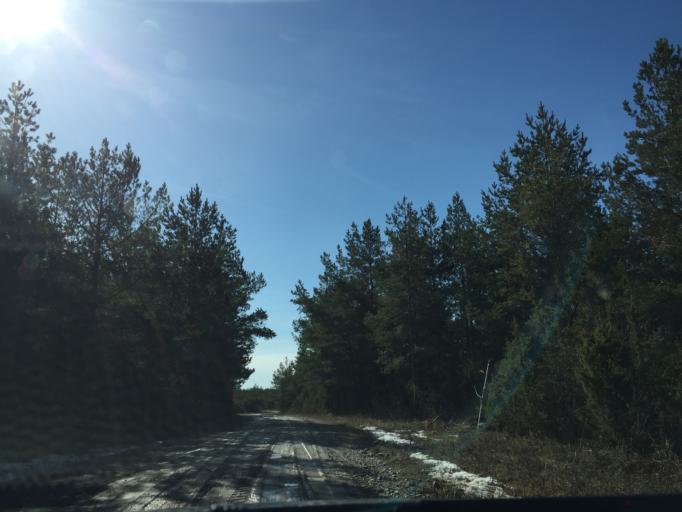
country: EE
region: Laeaene
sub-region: Haapsalu linn
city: Haapsalu
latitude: 58.6340
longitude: 23.5249
